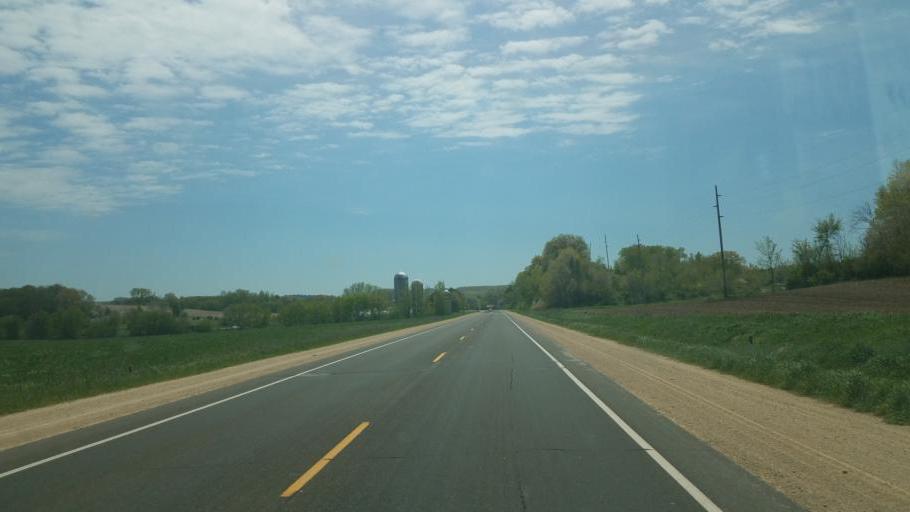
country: US
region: Wisconsin
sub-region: Monroe County
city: Tomah
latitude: 43.9355
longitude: -90.5030
